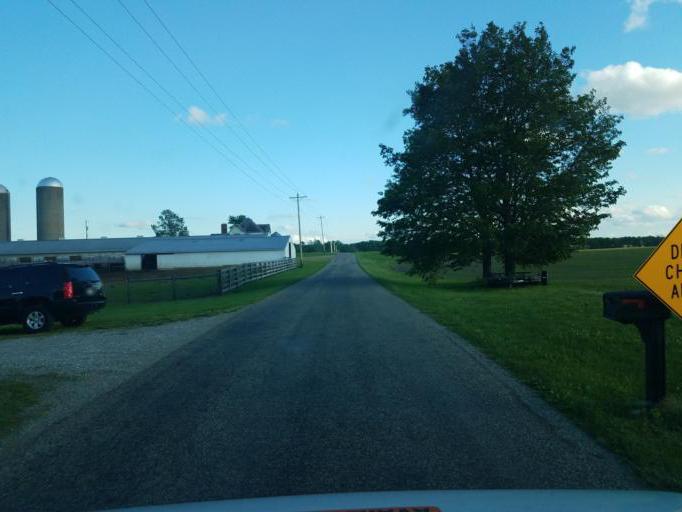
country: US
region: Ohio
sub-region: Knox County
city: Fredericktown
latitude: 40.4442
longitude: -82.6287
